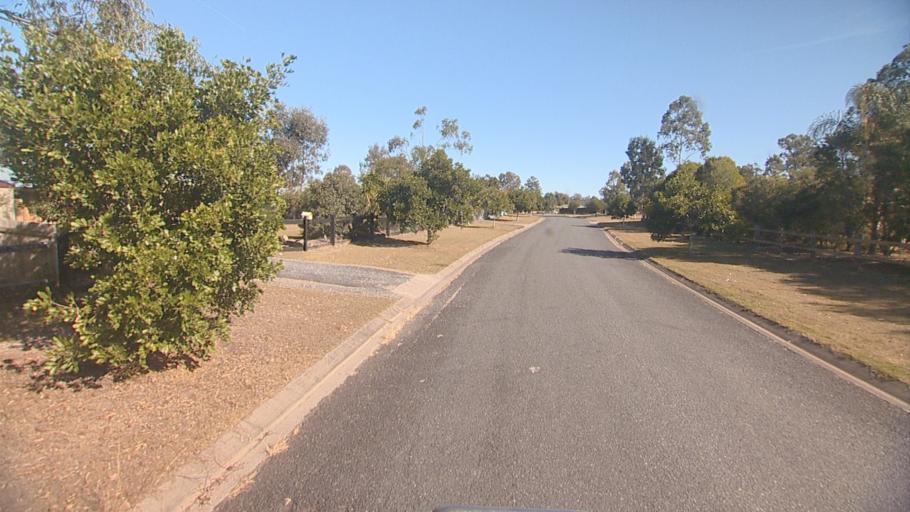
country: AU
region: Queensland
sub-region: Logan
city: North Maclean
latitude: -27.8001
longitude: 152.9689
